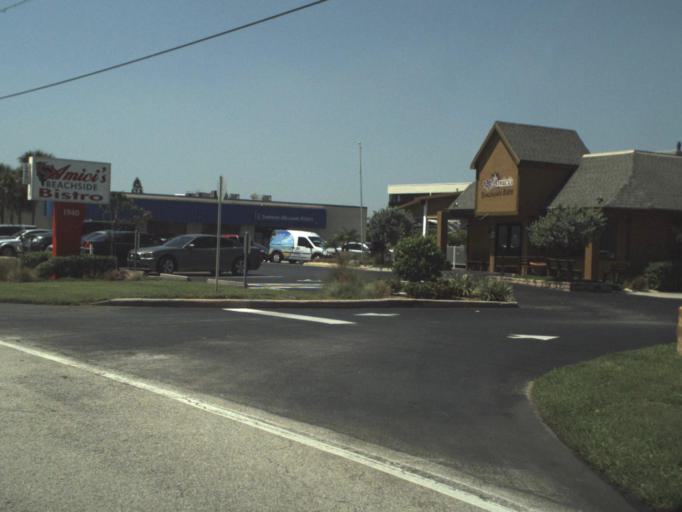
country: US
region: Florida
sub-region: Brevard County
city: Indian Harbour Beach
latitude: 28.1502
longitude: -80.5840
